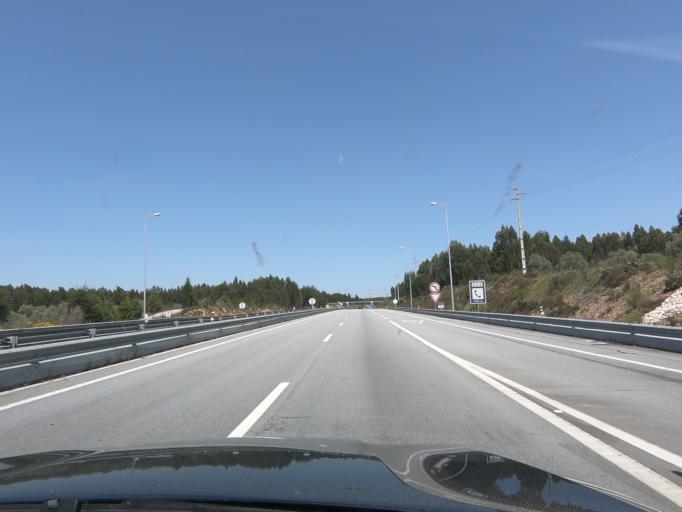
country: PT
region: Santarem
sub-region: Entroncamento
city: Entroncamento
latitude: 39.4958
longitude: -8.4416
